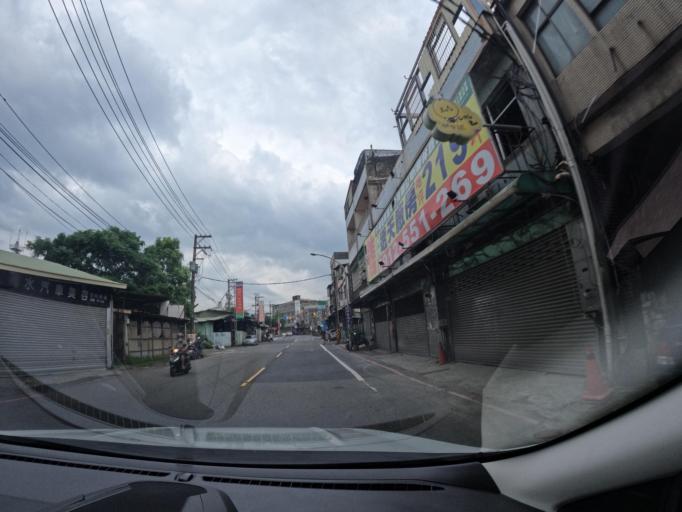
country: TW
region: Taiwan
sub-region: Taoyuan
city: Taoyuan
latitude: 24.9521
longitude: 121.3419
